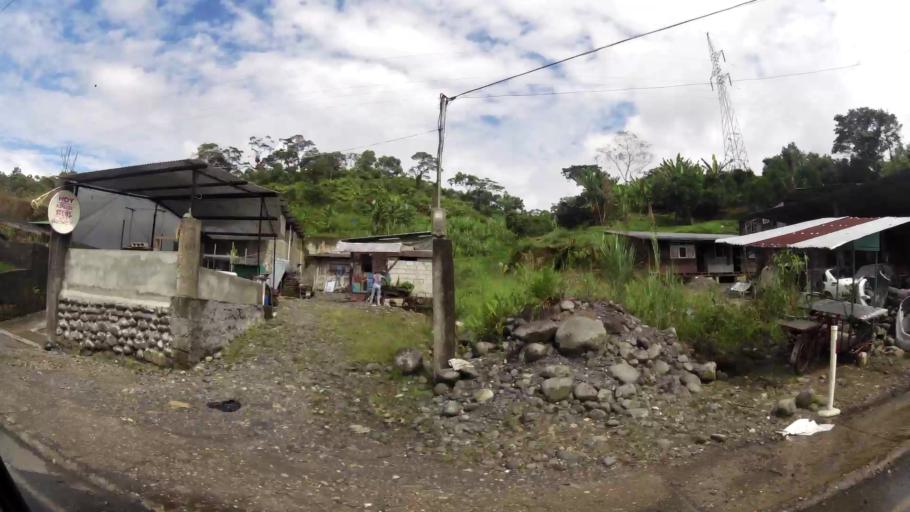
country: EC
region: Pastaza
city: Puyo
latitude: -1.4945
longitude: -78.0191
